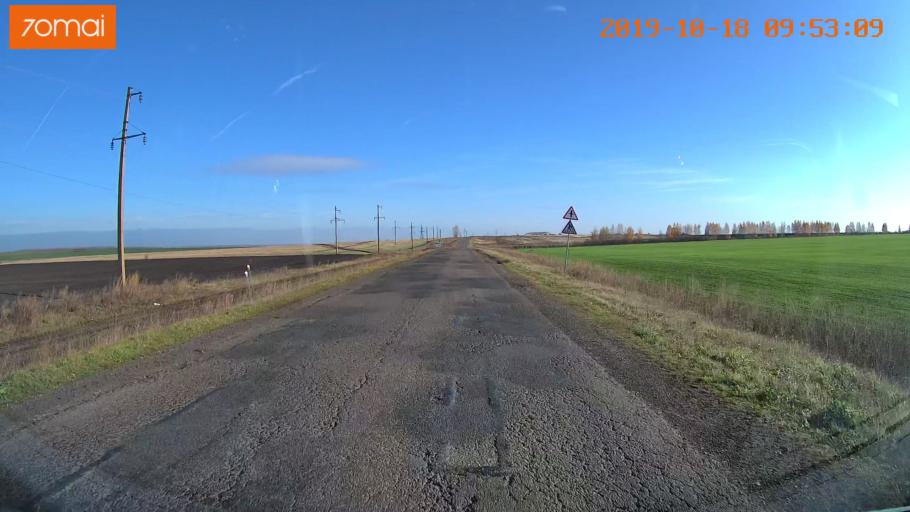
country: RU
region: Tula
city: Kazachka
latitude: 53.3582
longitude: 38.3234
